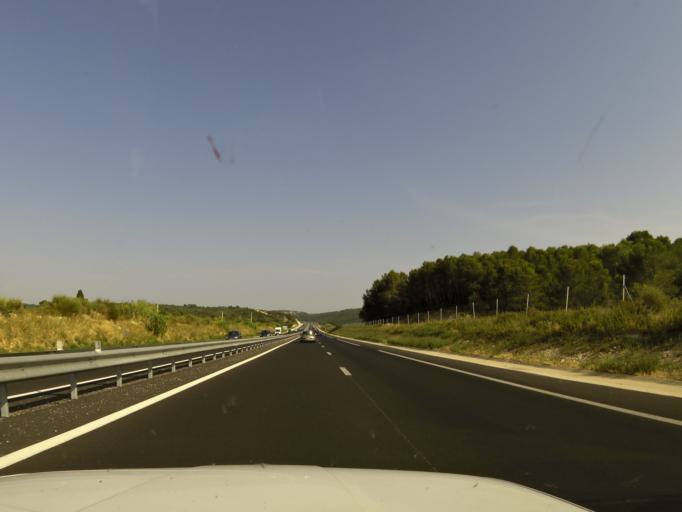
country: FR
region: Languedoc-Roussillon
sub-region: Departement de l'Herault
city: Gignac
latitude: 43.6363
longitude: 3.5825
